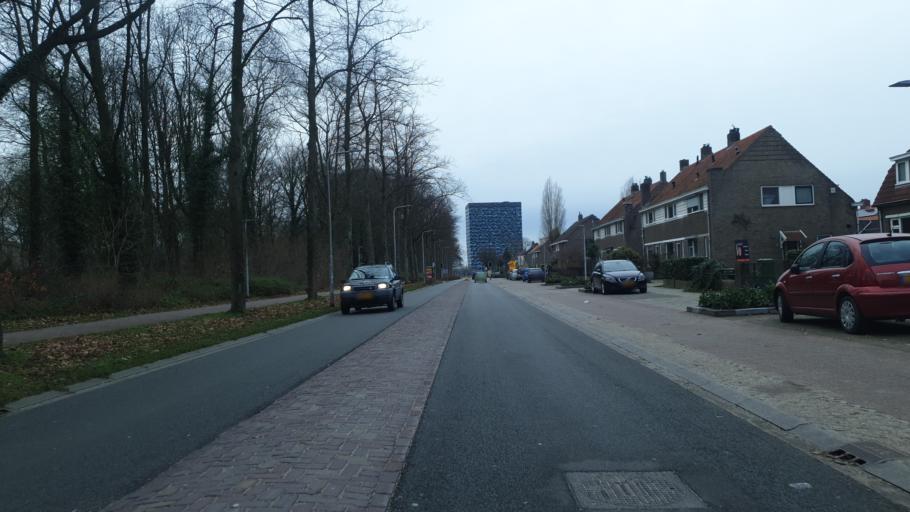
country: NL
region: Gelderland
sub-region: Gemeente Nijmegen
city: Nijmegen
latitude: 51.8295
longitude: 5.8333
